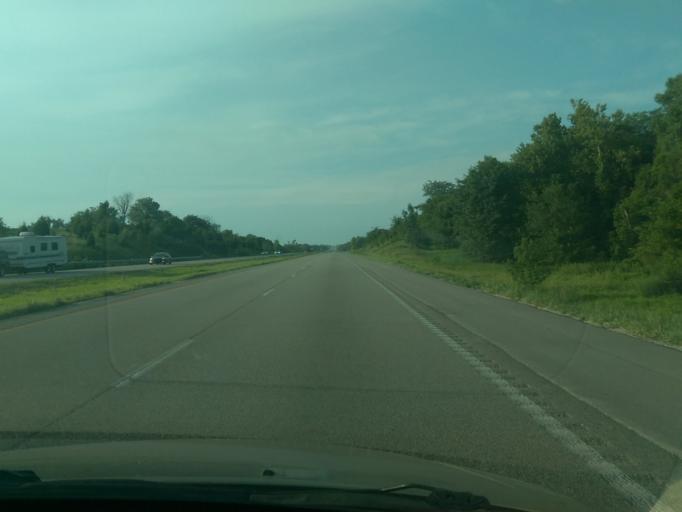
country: US
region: Missouri
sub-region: Platte County
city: Platte City
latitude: 39.4392
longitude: -94.7892
